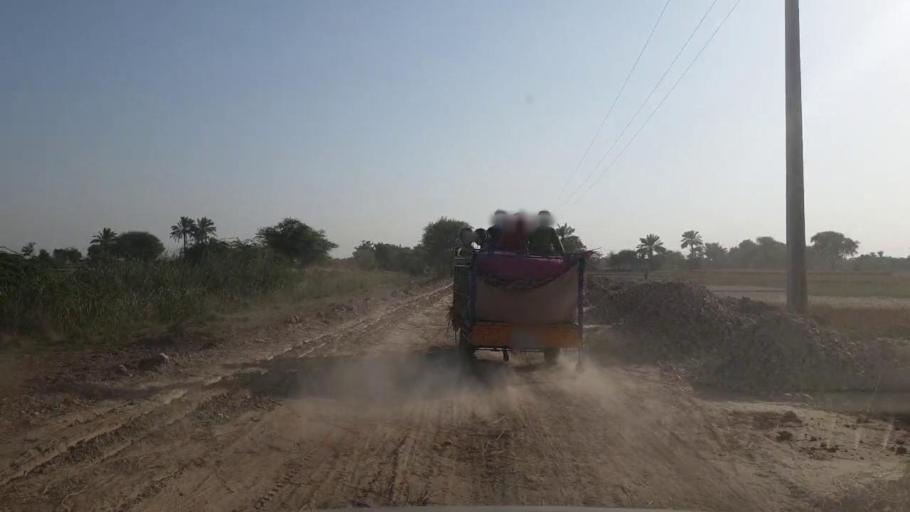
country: PK
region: Sindh
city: Talhar
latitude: 24.9236
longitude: 68.7471
